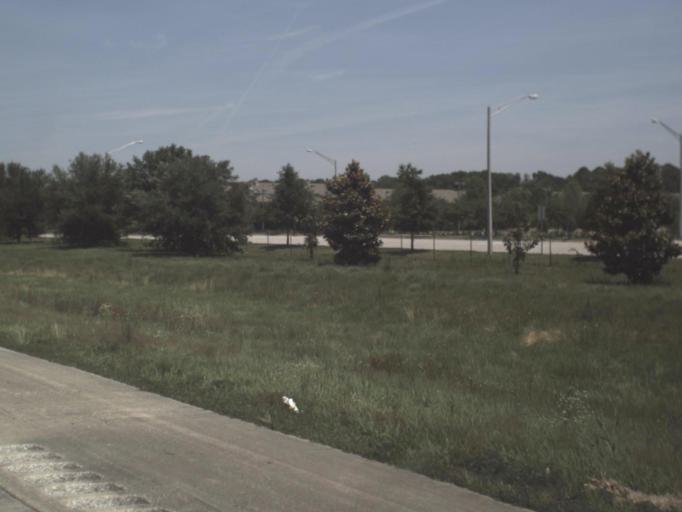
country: US
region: Florida
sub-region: Saint Johns County
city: Palm Valley
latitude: 30.2071
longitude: -81.5137
